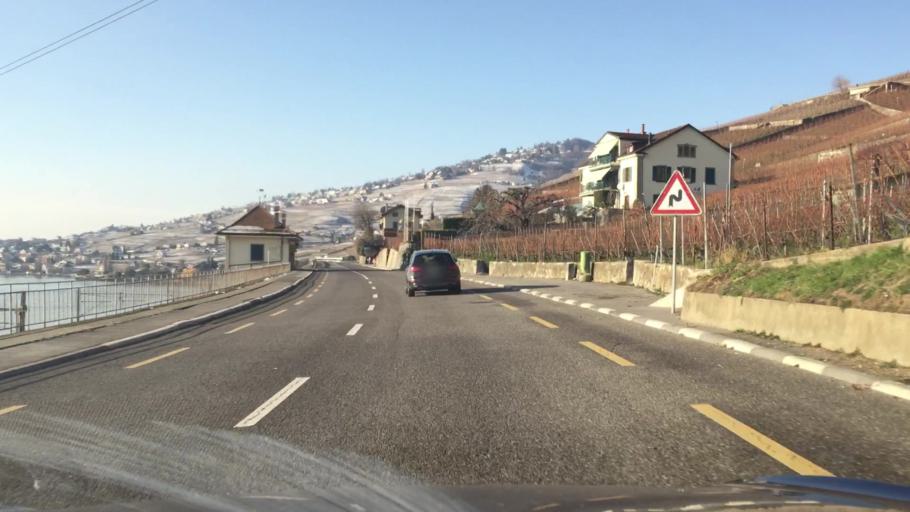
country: CH
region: Vaud
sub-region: Lavaux-Oron District
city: Cully
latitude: 46.4864
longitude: 6.7525
